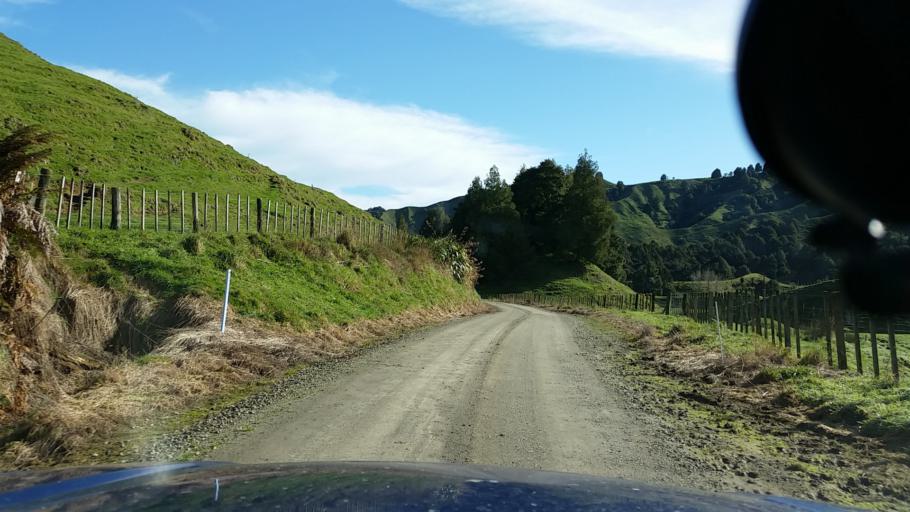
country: NZ
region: Taranaki
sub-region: New Plymouth District
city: Waitara
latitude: -39.0521
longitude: 174.7700
